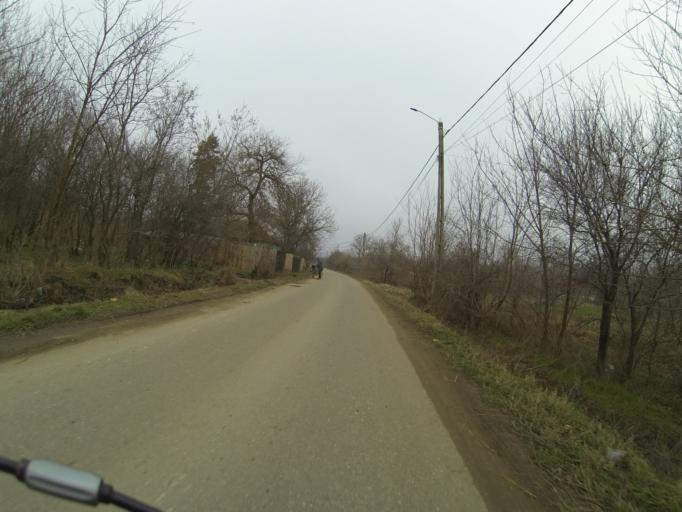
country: RO
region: Mehedinti
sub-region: Comuna Balacita
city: Gvardinita
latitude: 44.3950
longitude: 23.1449
